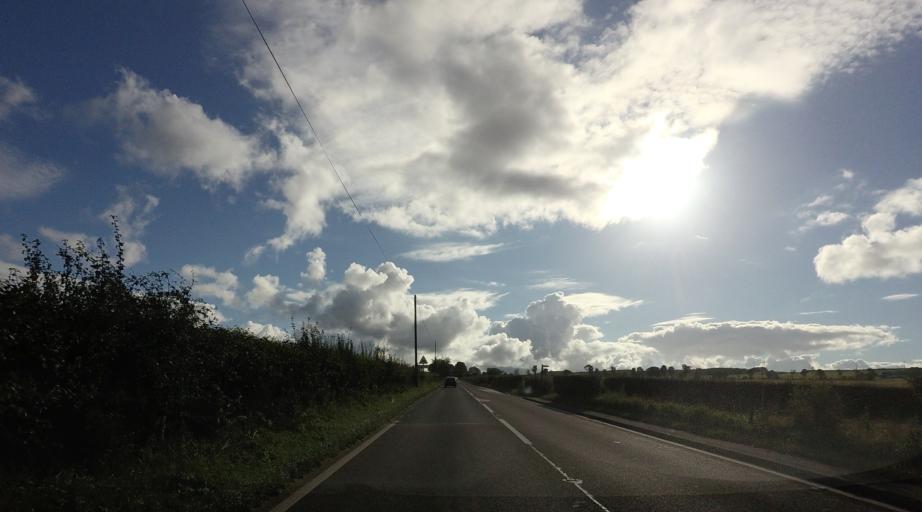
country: GB
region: Scotland
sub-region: Fife
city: Freuchie
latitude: 56.2419
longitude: -3.1537
